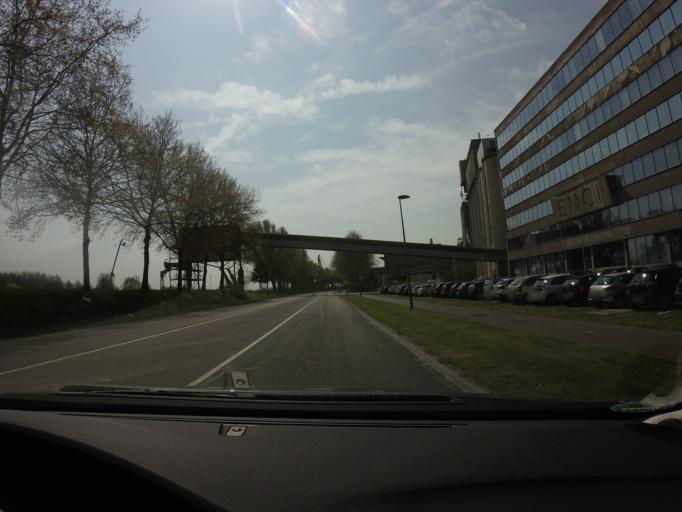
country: NL
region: Limburg
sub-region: Gemeente Maastricht
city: Maastricht
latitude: 50.8228
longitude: 5.6963
